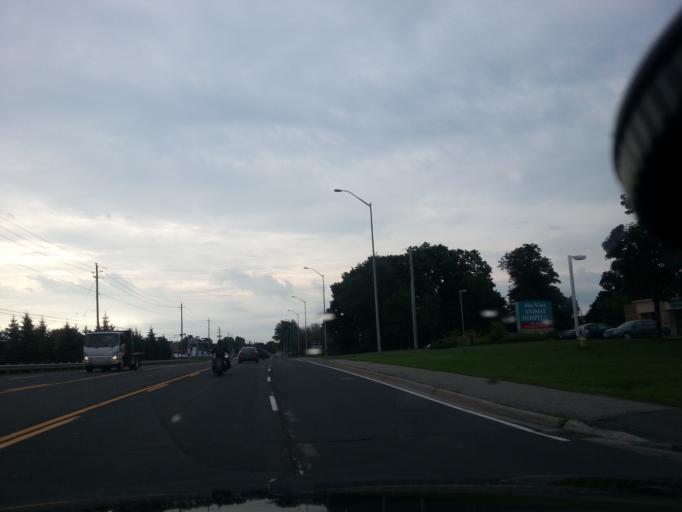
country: CA
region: Ontario
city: Ottawa
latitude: 45.3536
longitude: -75.6389
